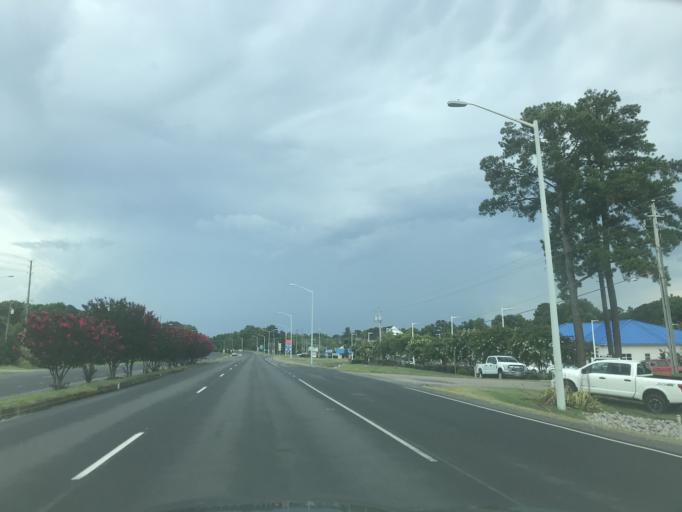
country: US
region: North Carolina
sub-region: Johnston County
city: Clayton
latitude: 35.6497
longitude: -78.4691
